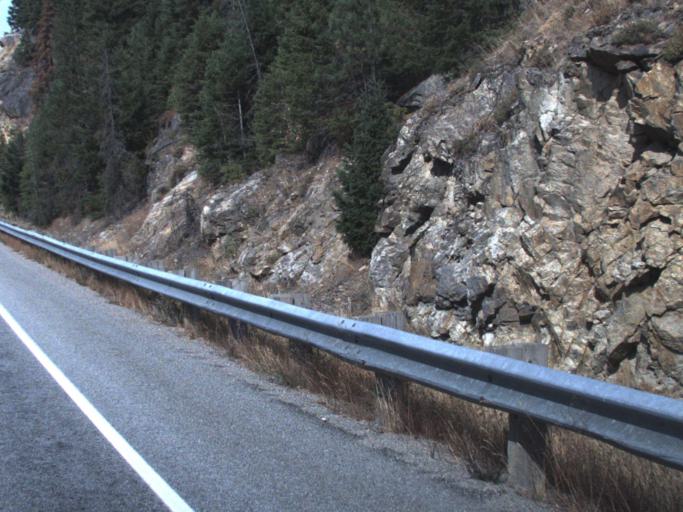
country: US
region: Washington
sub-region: Pend Oreille County
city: Newport
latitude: 48.2259
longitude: -117.2917
